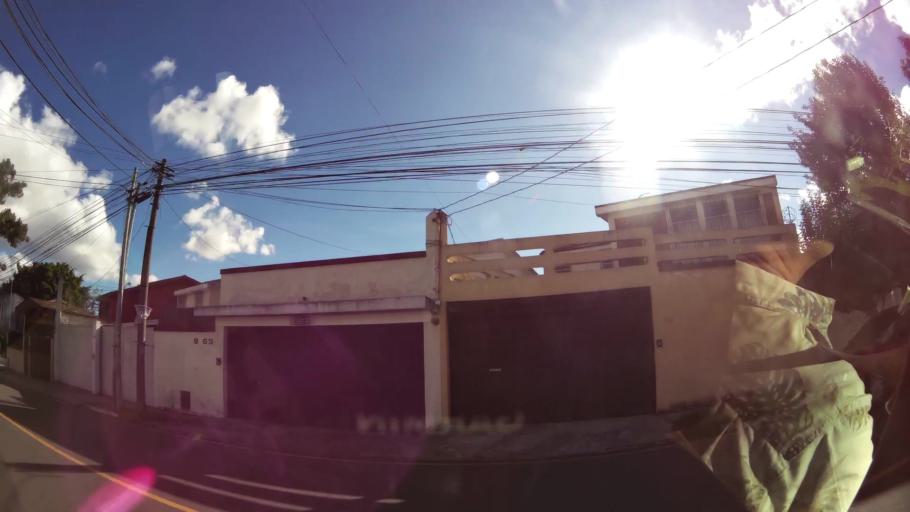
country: GT
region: Guatemala
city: Guatemala City
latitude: 14.6018
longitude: -90.5565
